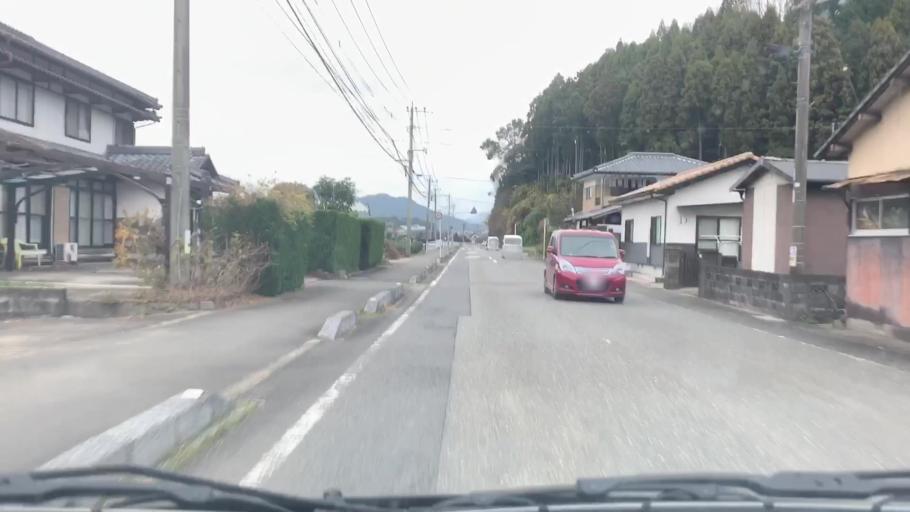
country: JP
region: Saga Prefecture
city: Kashima
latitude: 33.1173
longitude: 130.0641
